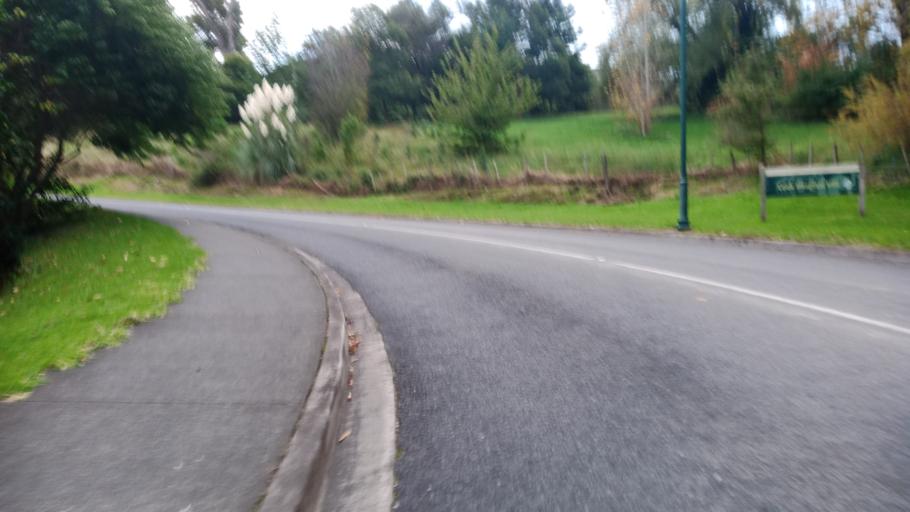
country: NZ
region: Gisborne
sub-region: Gisborne District
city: Gisborne
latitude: -38.6435
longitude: 178.0177
